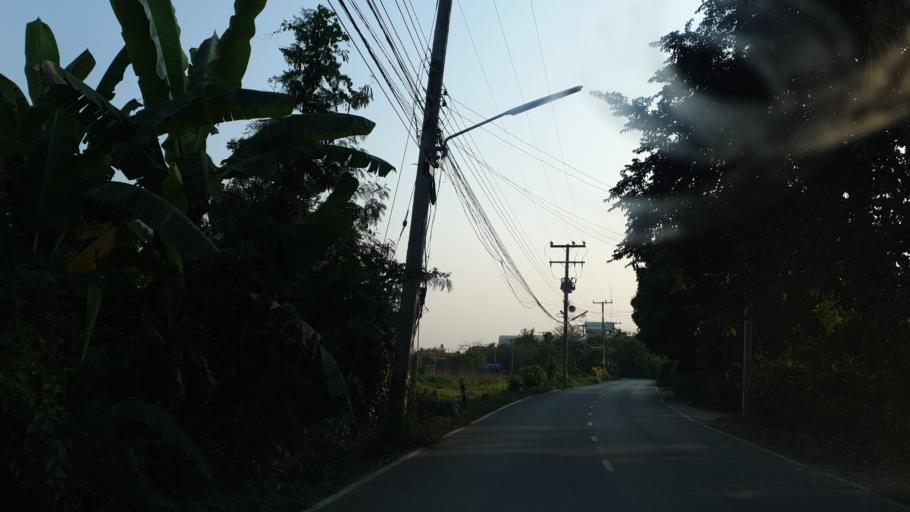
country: TH
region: Chiang Mai
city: Saraphi
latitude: 18.7102
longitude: 99.0274
